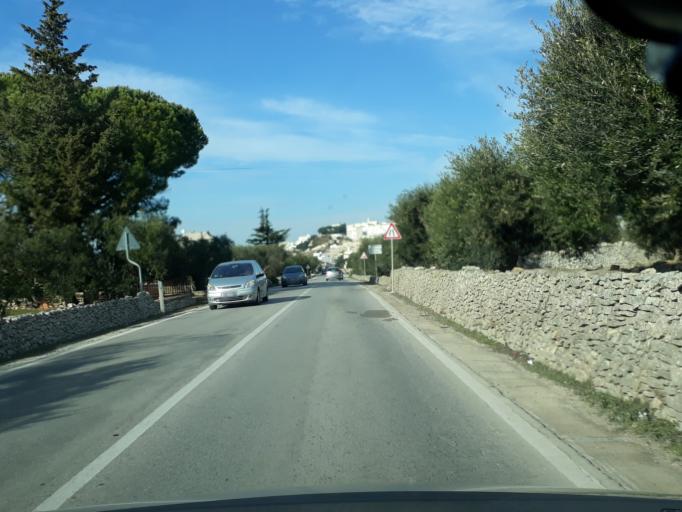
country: IT
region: Apulia
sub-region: Provincia di Bari
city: Locorotondo
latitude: 40.7430
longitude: 17.3321
